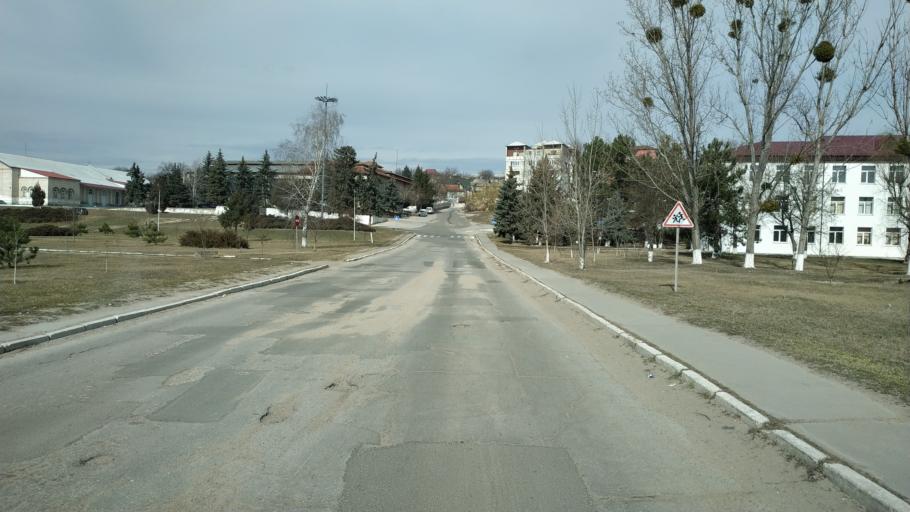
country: MD
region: Chisinau
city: Vatra
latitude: 47.0932
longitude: 28.6659
